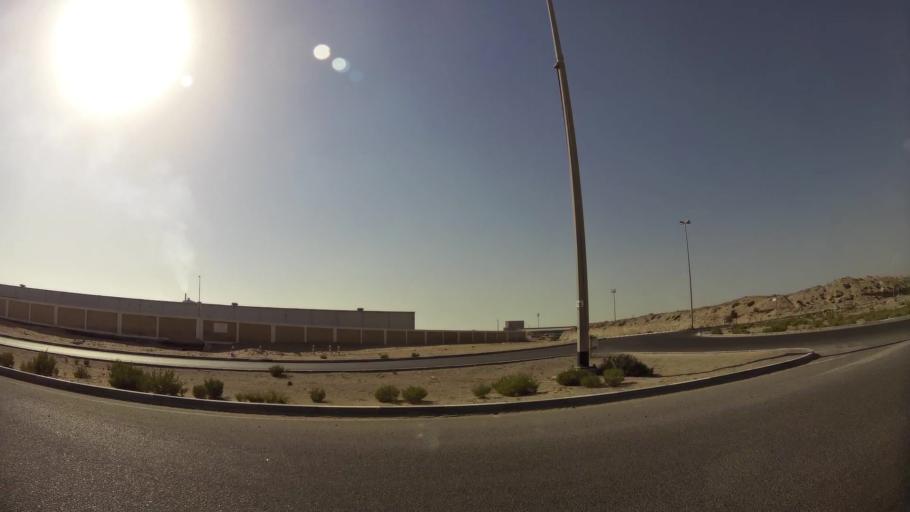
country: AE
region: Dubai
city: Dubai
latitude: 24.9950
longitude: 55.1255
